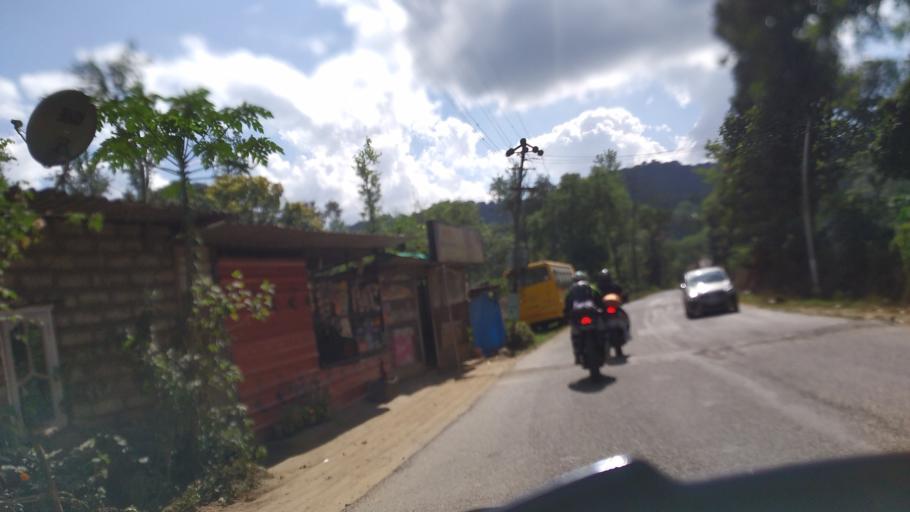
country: IN
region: Karnataka
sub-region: Kodagu
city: Ponnampet
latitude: 11.9656
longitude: 76.0571
